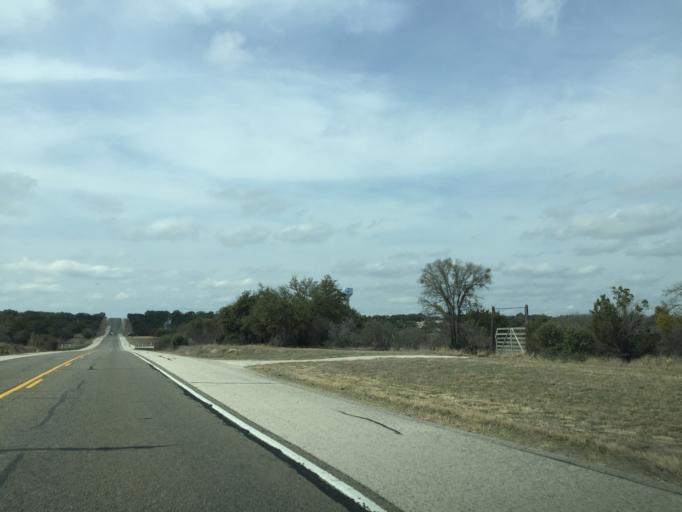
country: US
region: Texas
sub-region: Llano County
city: Horseshoe Bay
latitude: 30.5127
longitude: -98.3749
